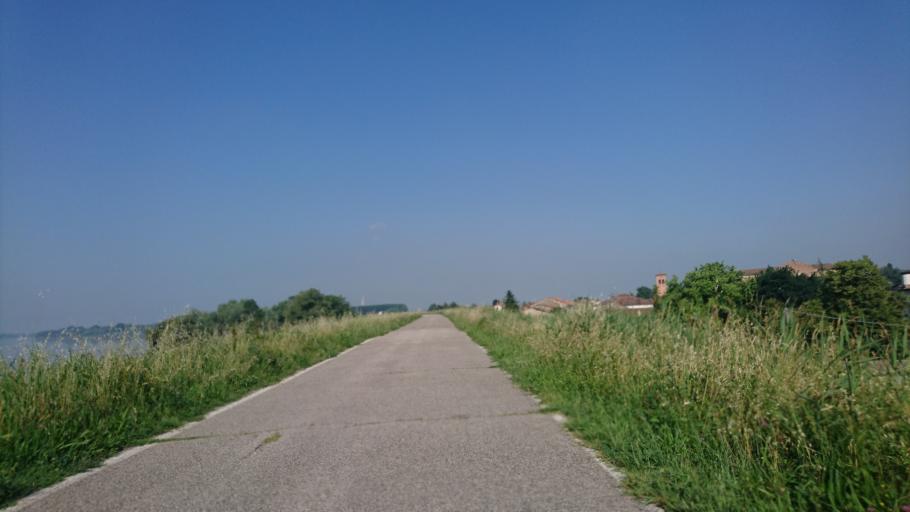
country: IT
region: Veneto
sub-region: Provincia di Rovigo
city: Melara
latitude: 45.0609
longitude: 11.2045
